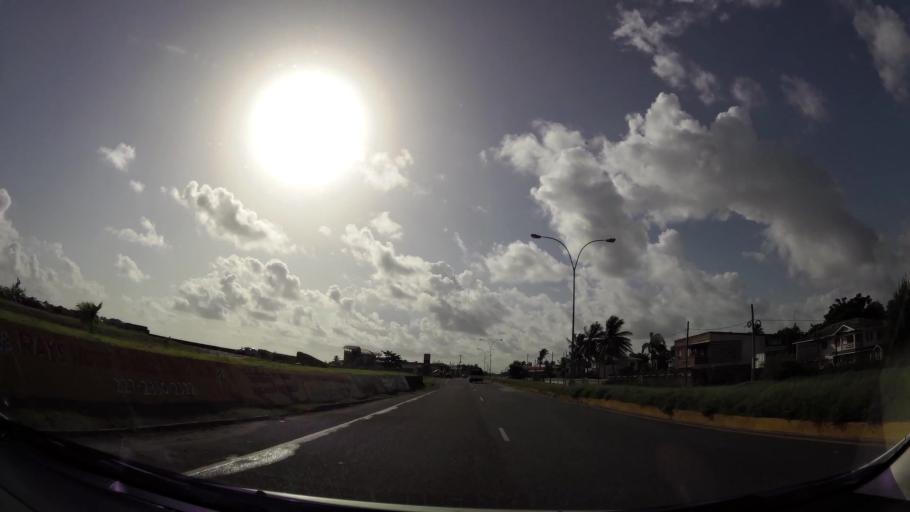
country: GY
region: Demerara-Mahaica
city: Georgetown
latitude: 6.8225
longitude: -58.1018
